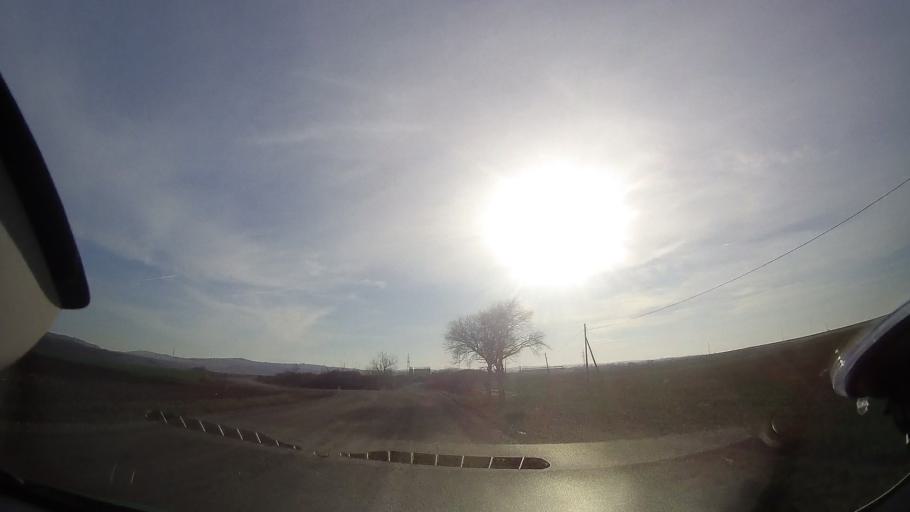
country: RO
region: Bihor
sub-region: Comuna Ciuhoiu
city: Ciuhoiu
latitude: 47.2198
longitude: 22.1341
